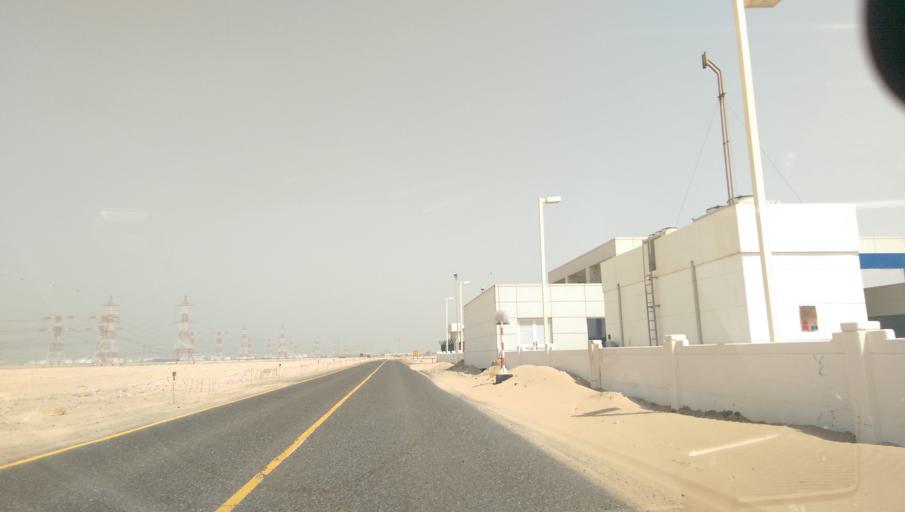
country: AE
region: Abu Dhabi
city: Abu Dhabi
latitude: 24.2964
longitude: 54.5403
